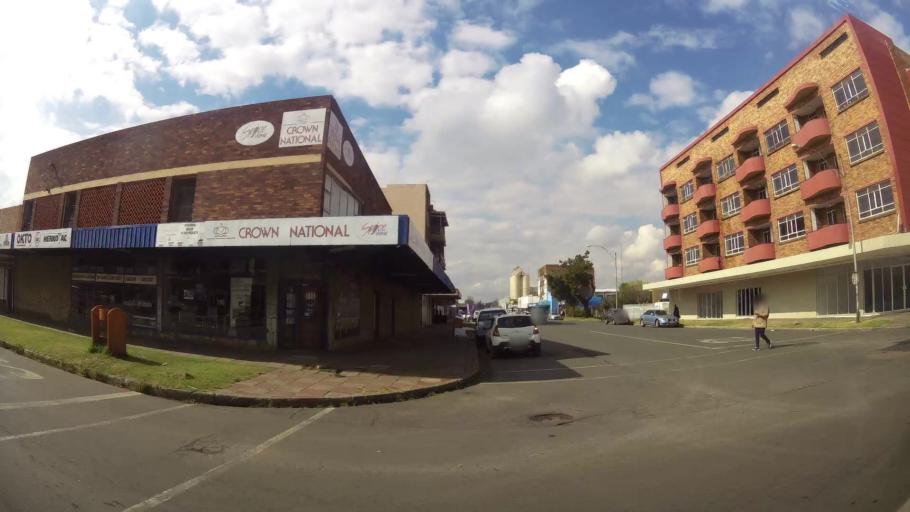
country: ZA
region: Gauteng
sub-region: Sedibeng District Municipality
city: Vereeniging
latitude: -26.6693
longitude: 27.9306
